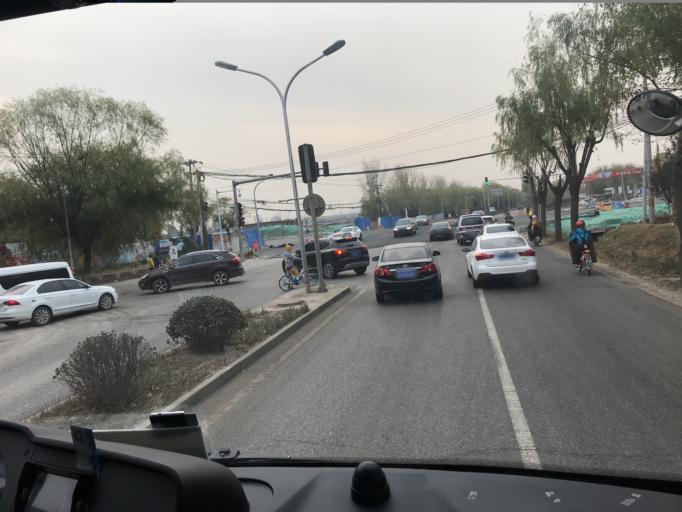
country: CN
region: Beijing
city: Sujiatuo
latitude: 40.0920
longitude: 116.2094
